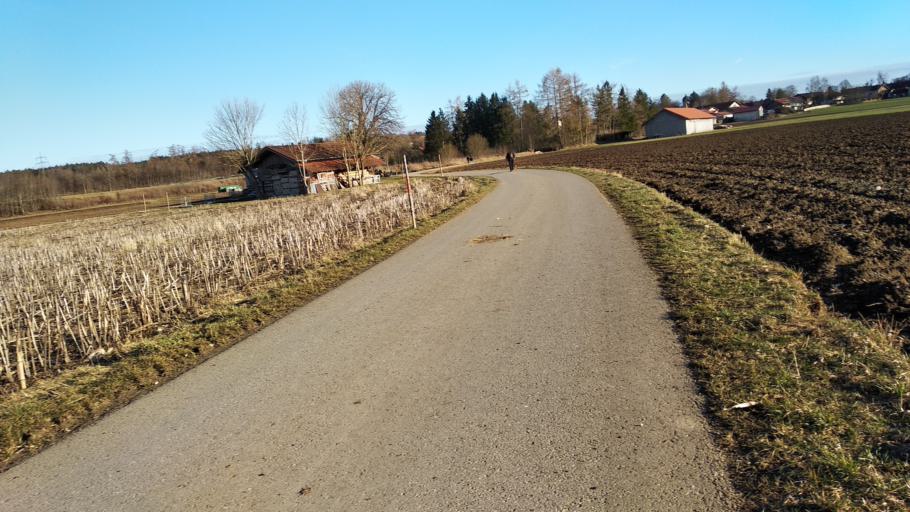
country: DE
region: Bavaria
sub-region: Upper Bavaria
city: Aying
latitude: 47.9774
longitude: 11.7745
